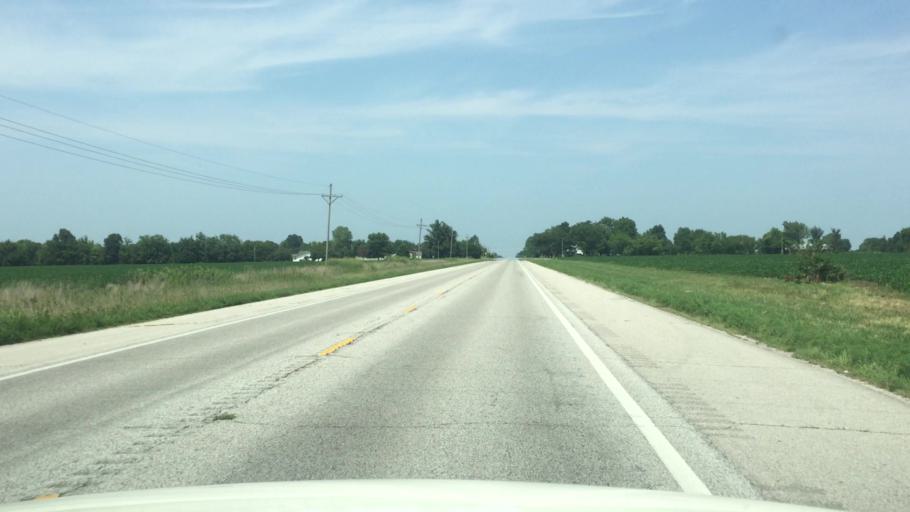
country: US
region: Kansas
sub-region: Cherokee County
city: Galena
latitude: 37.0973
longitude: -94.7043
